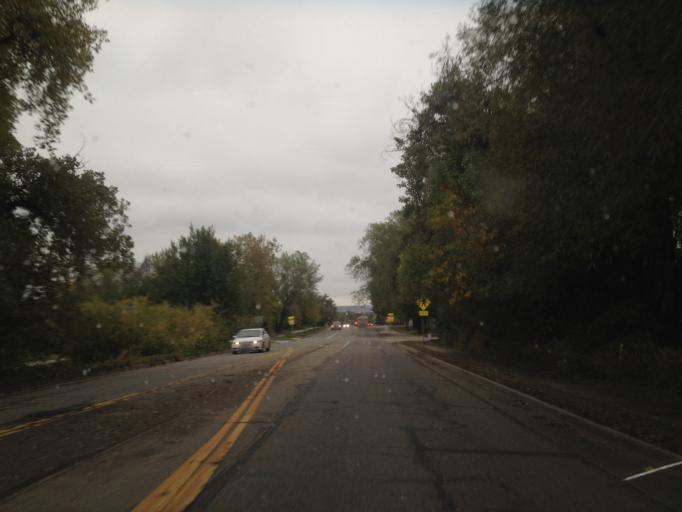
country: US
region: Colorado
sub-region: Boulder County
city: Boulder
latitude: 40.0318
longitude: -105.2347
